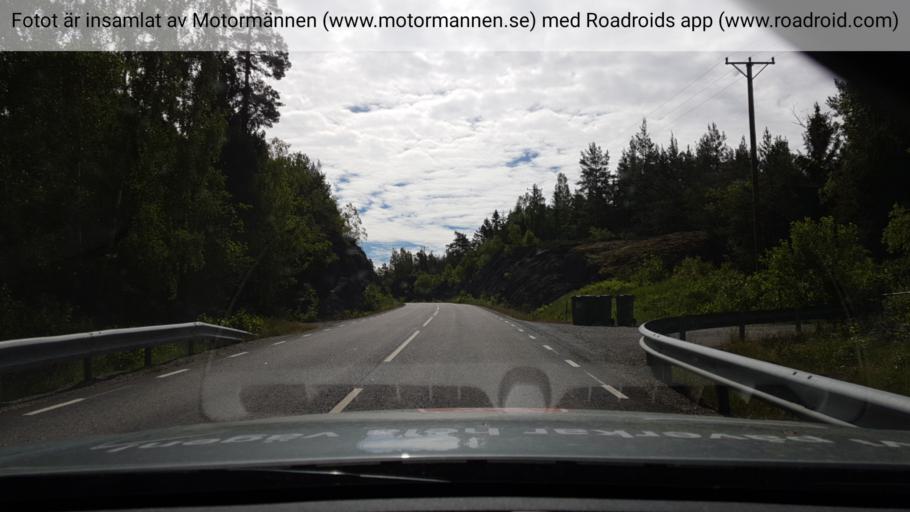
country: SE
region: Stockholm
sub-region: Nynashamns Kommun
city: Nynashamn
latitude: 58.9513
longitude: 18.0018
